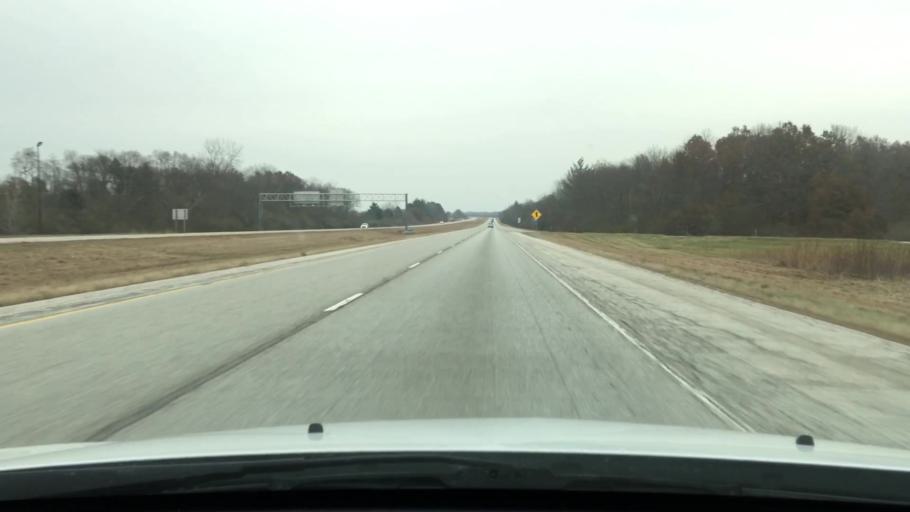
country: US
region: Illinois
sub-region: Morgan County
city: South Jacksonville
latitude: 39.6802
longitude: -90.2914
